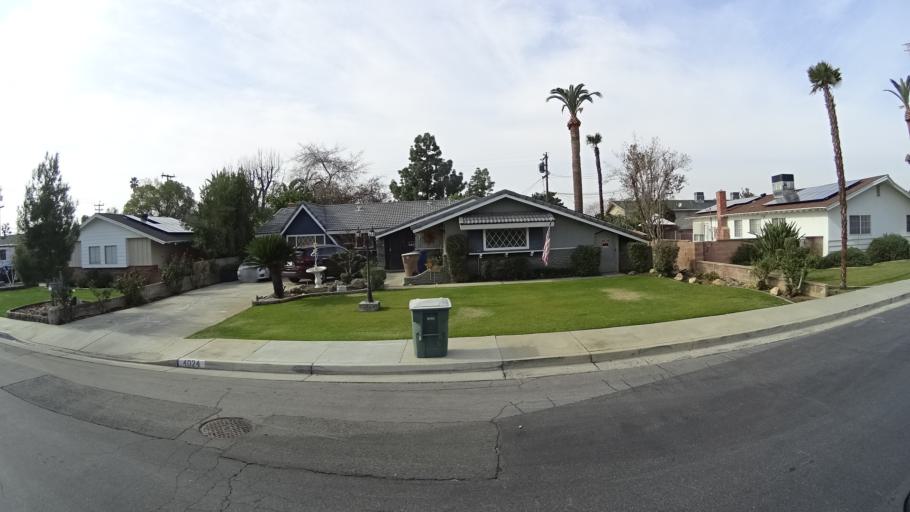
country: US
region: California
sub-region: Kern County
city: Oildale
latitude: 35.4100
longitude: -118.9631
